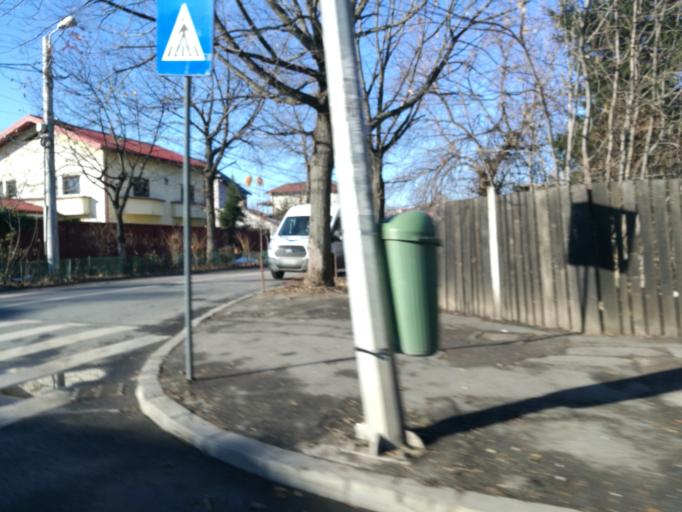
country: RO
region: Ilfov
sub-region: Comuna Chiajna
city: Rosu
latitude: 44.4897
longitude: 26.0542
